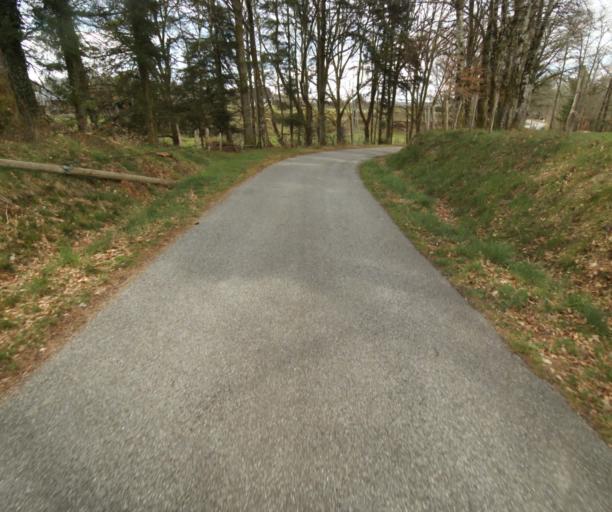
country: FR
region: Limousin
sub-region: Departement de la Correze
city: Correze
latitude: 45.3877
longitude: 1.8964
